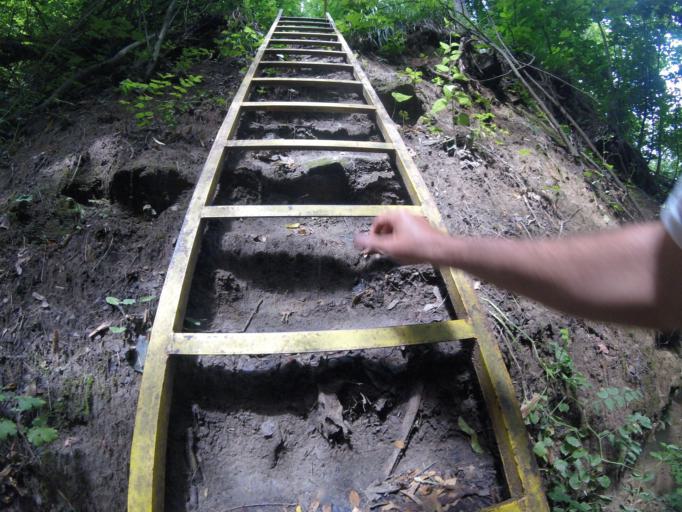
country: HU
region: Zala
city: Nagykanizsa
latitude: 46.5603
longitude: 17.0238
